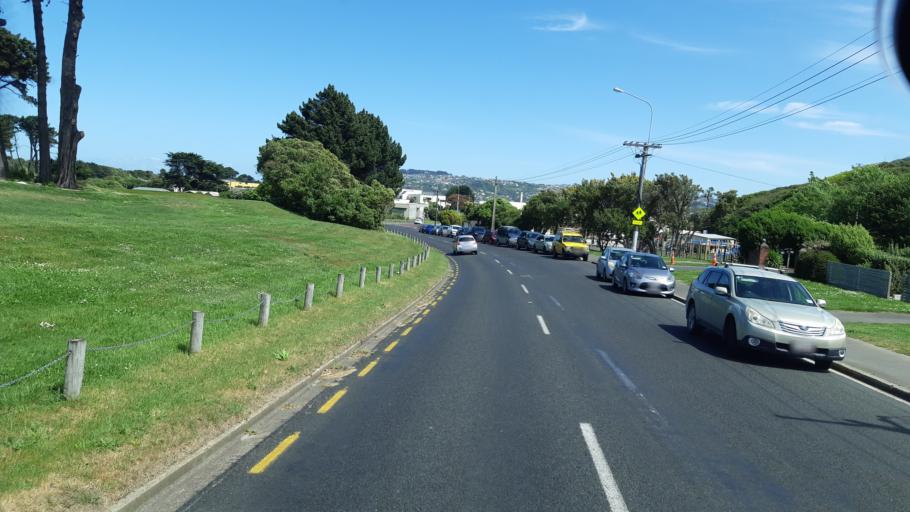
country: NZ
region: Otago
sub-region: Dunedin City
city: Dunedin
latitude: -45.9030
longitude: 170.5271
